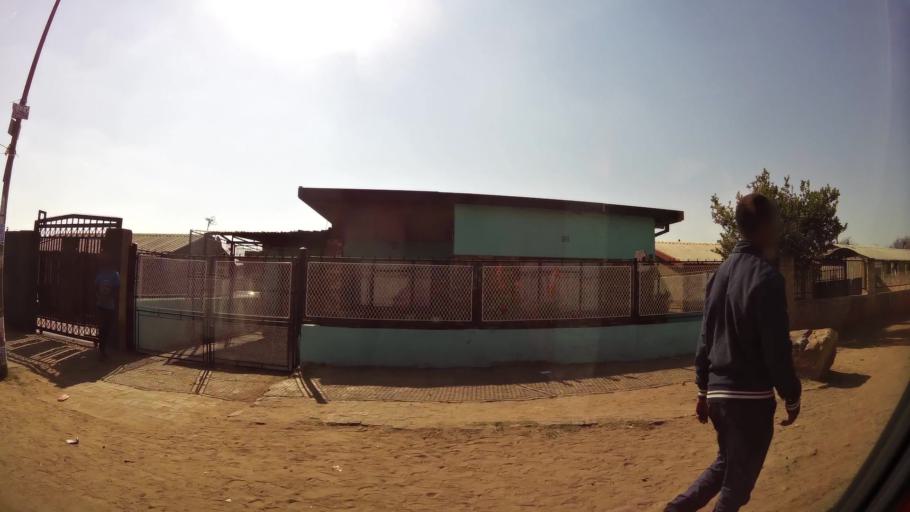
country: ZA
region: Gauteng
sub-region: City of Johannesburg Metropolitan Municipality
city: Johannesburg
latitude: -26.2441
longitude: 27.9544
